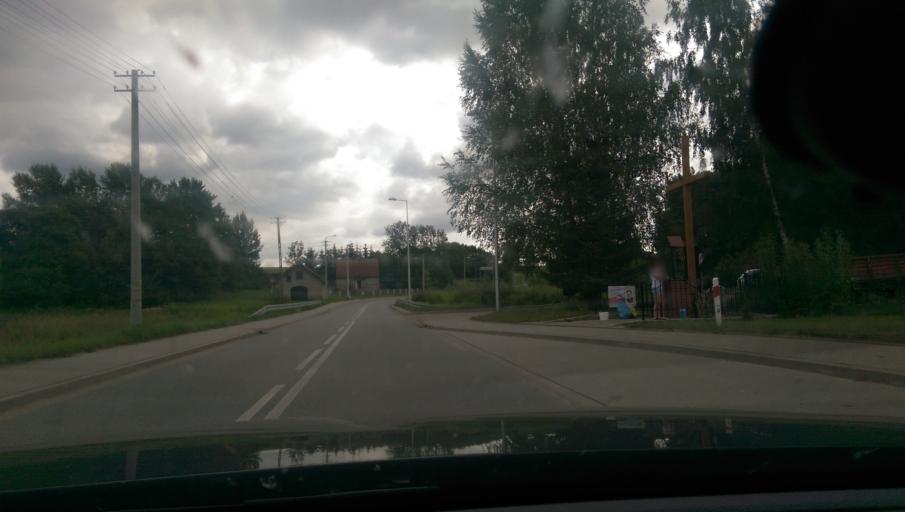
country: PL
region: Warmian-Masurian Voivodeship
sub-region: Powiat goldapski
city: Banie Mazurskie
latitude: 54.2317
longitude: 22.0973
